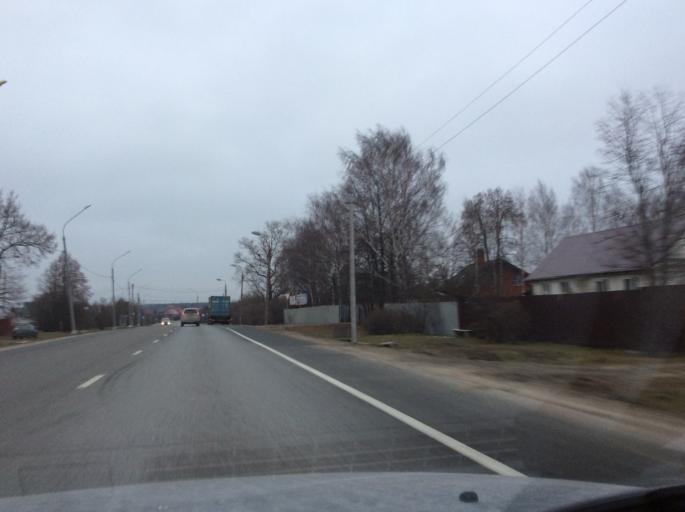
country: RU
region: Moskovskaya
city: Troitsk
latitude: 55.3678
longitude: 37.2002
